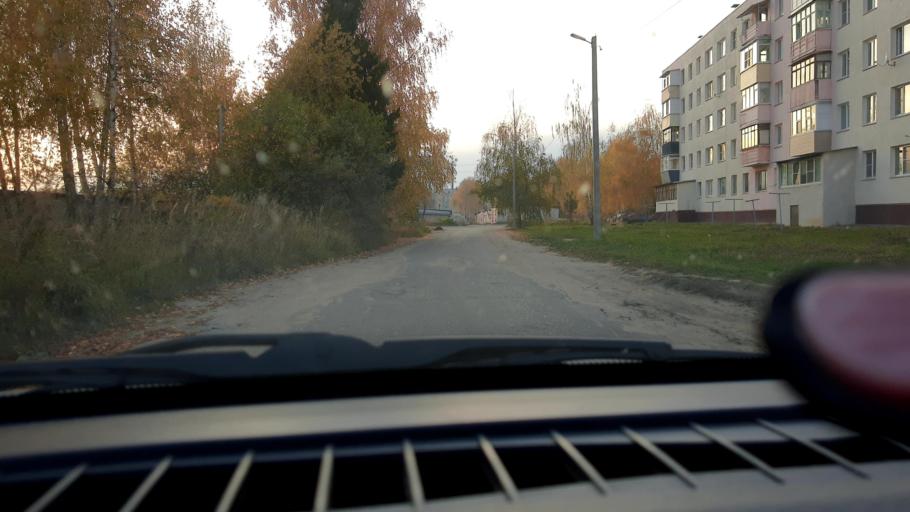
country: RU
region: Nizjnij Novgorod
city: Gorodets
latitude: 56.6370
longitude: 43.4856
